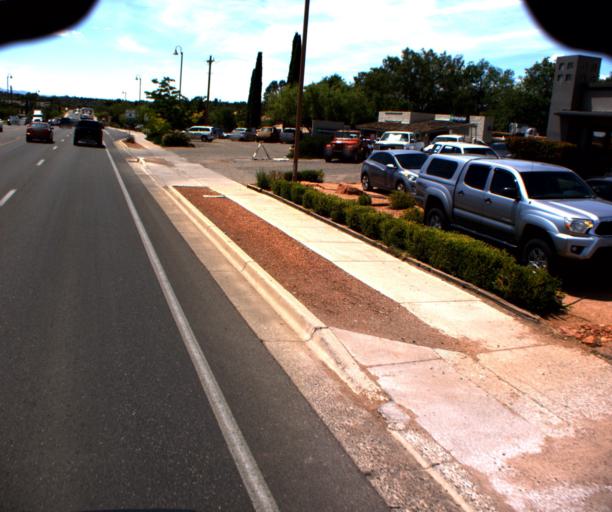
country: US
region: Arizona
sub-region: Yavapai County
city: West Sedona
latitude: 34.8638
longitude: -111.7969
